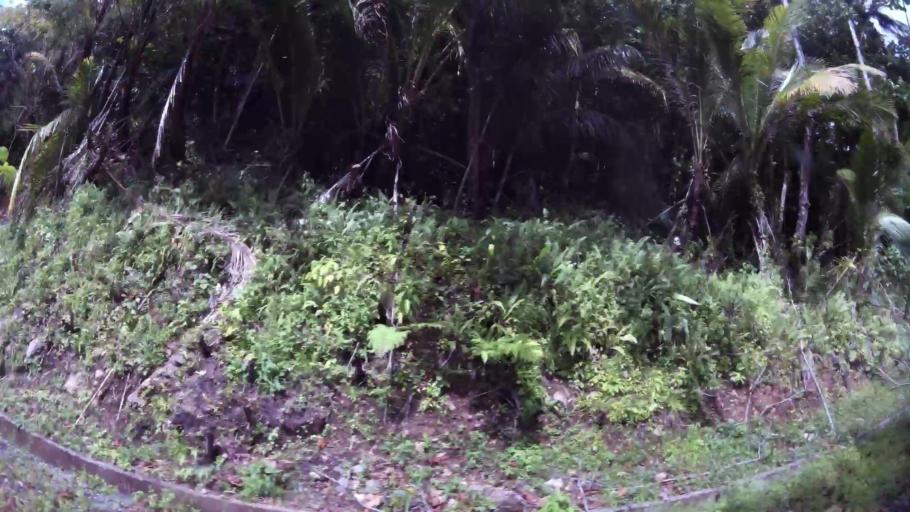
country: DM
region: Saint John
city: Portsmouth
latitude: 15.6107
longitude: -61.4486
